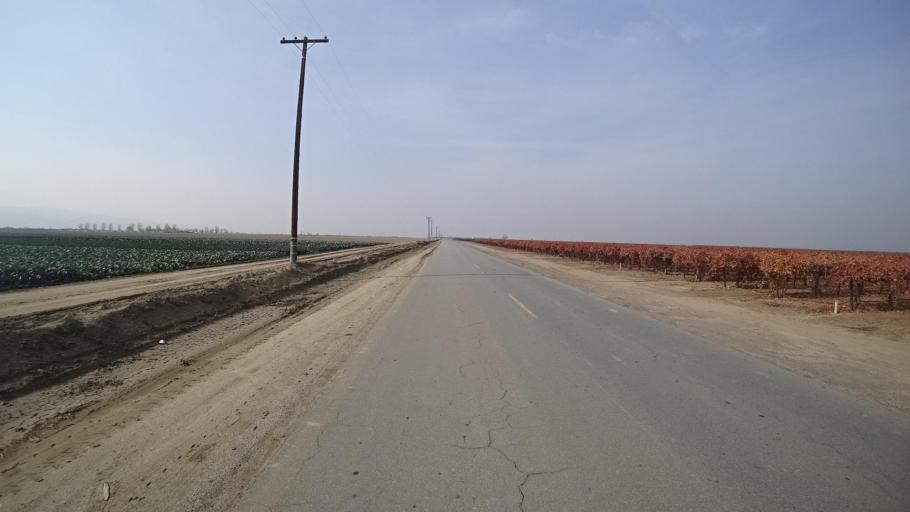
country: US
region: California
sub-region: Kern County
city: Weedpatch
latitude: 35.0753
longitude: -118.9474
